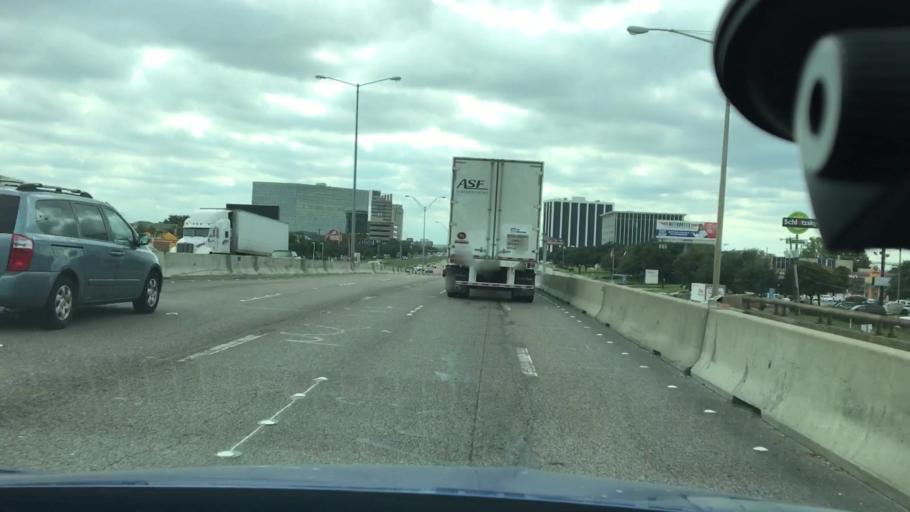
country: US
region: Texas
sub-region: Dallas County
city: University Park
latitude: 32.8265
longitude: -96.8724
